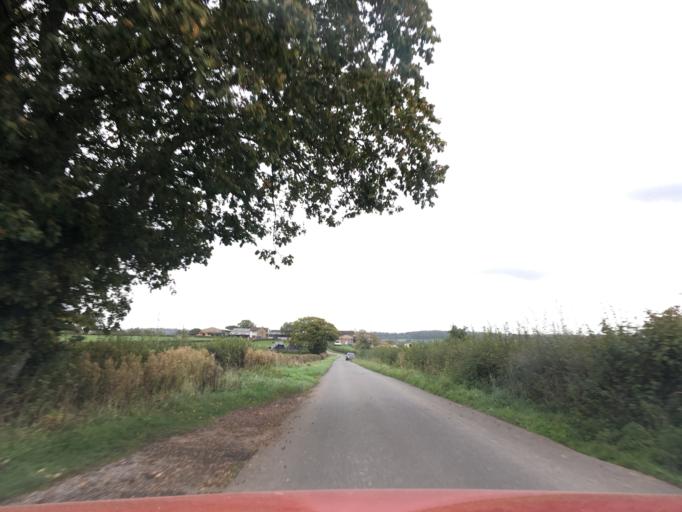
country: GB
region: England
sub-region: South Gloucestershire
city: Wickwar
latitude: 51.5984
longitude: -2.3873
